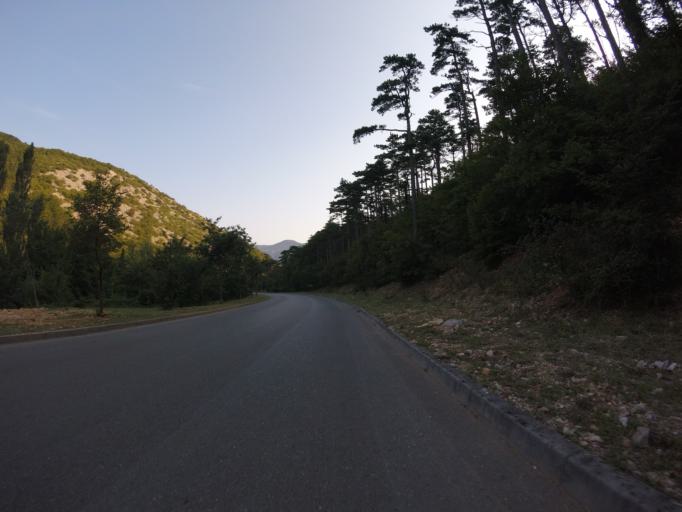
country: HR
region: Primorsko-Goranska
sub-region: Grad Crikvenica
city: Crikvenica
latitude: 45.1865
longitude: 14.7003
